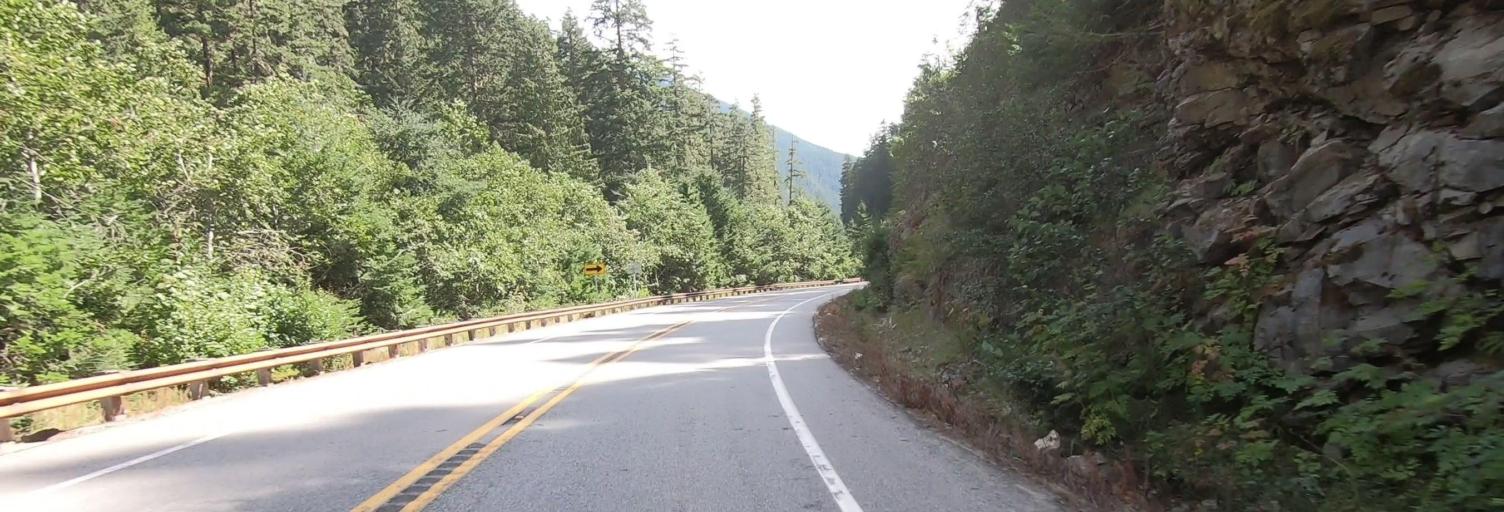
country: US
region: Washington
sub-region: Snohomish County
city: Darrington
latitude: 48.6868
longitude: -120.9058
